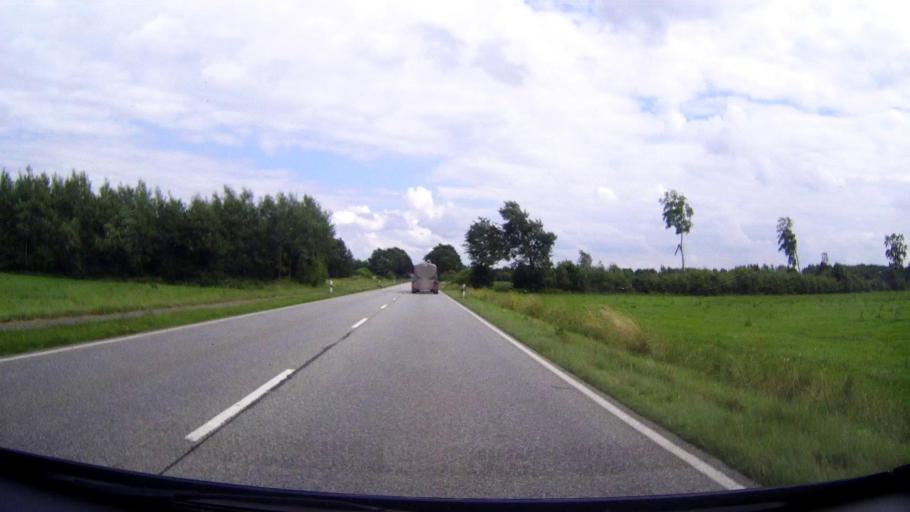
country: DE
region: Schleswig-Holstein
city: Wasbek
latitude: 54.0711
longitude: 9.8746
